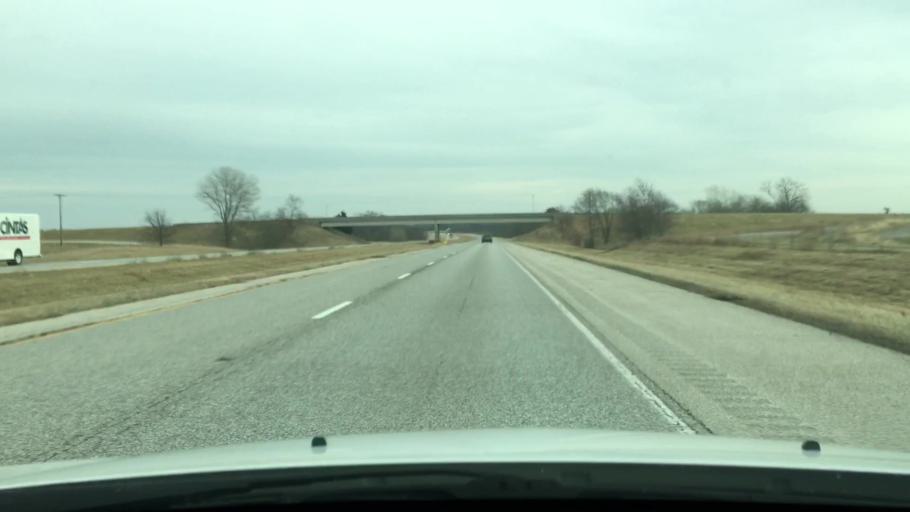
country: US
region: Illinois
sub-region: Pike County
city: Griggsville
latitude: 39.6781
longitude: -90.7065
